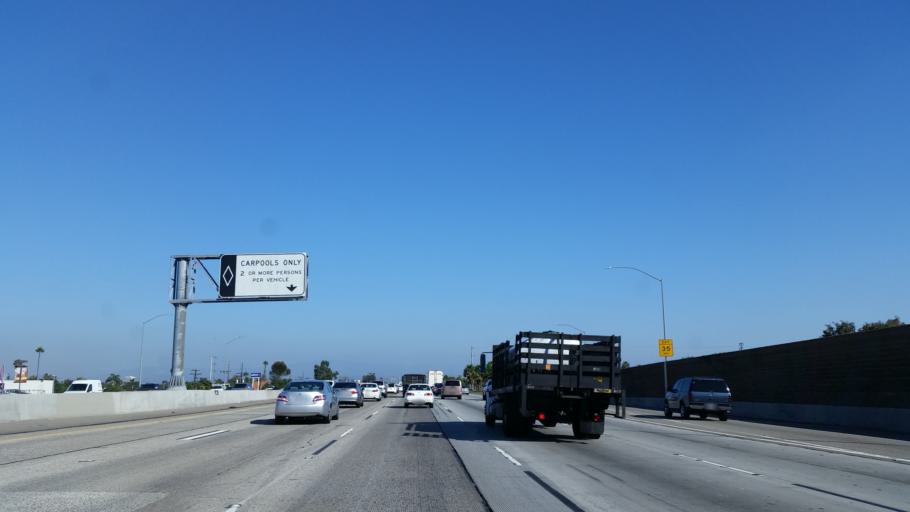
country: US
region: California
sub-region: Orange County
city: Garden Grove
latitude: 33.7659
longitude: -117.9413
